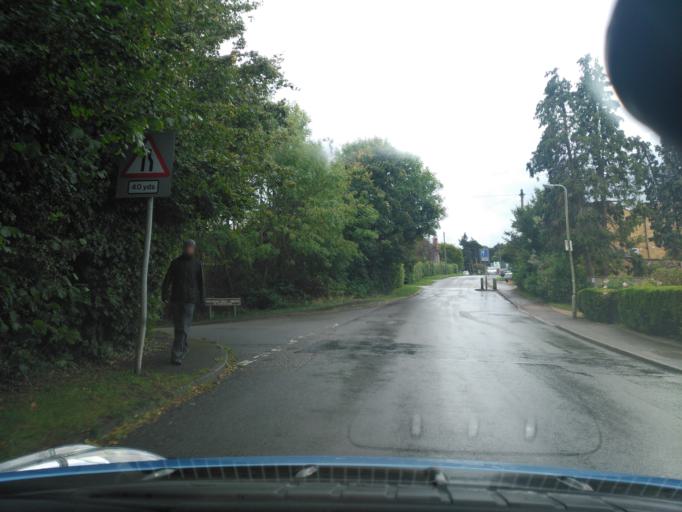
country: GB
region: England
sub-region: Oxfordshire
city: Wheatley
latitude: 51.7451
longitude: -1.1400
